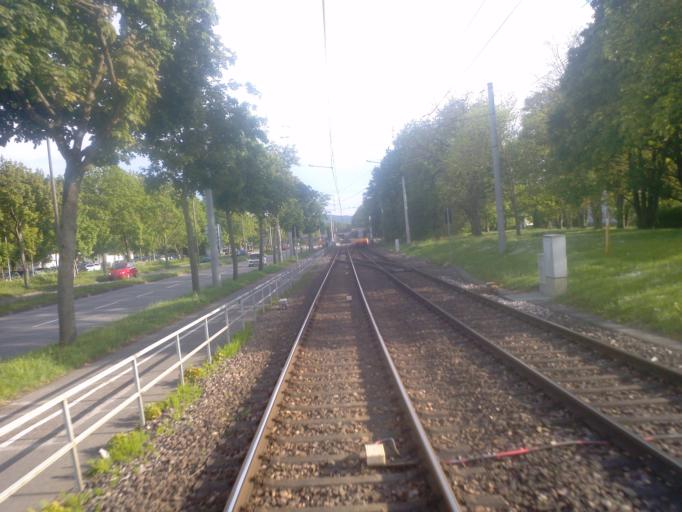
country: DE
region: Baden-Wuerttemberg
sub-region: Karlsruhe Region
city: Karlsruhe
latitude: 48.9865
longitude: 8.4034
